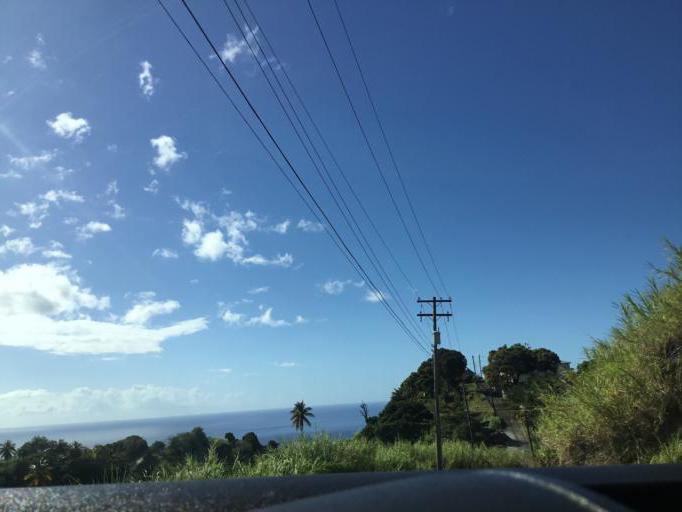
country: VC
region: Saint David
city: Chateaubelair
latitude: 13.2755
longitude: -61.2489
